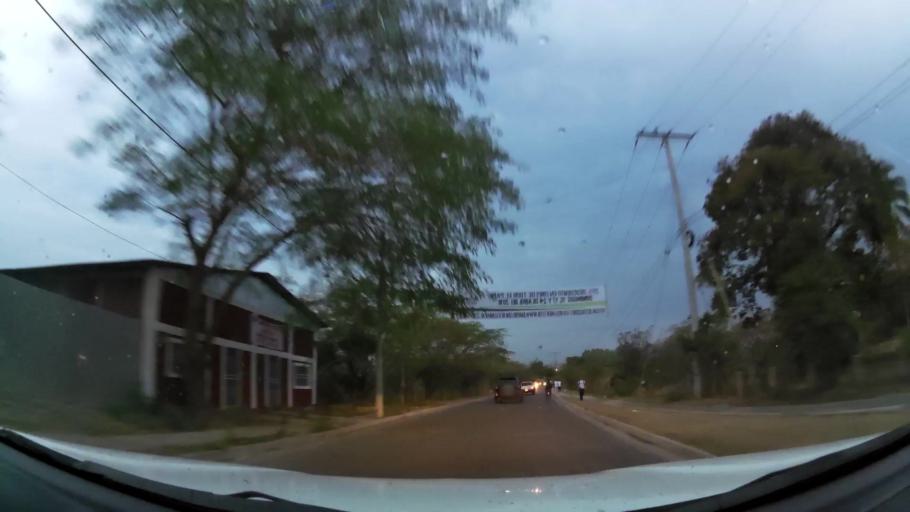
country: NI
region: Esteli
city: Esteli
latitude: 13.1010
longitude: -86.3572
